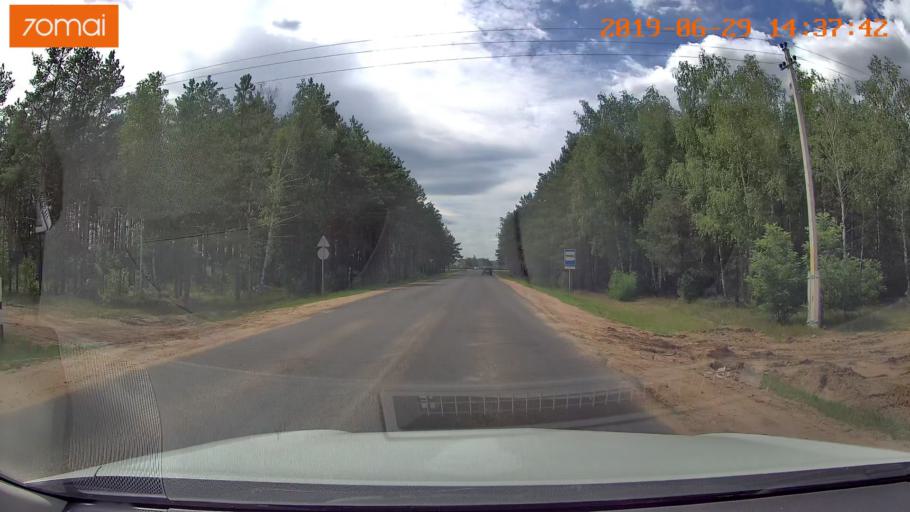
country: BY
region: Minsk
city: Starobin
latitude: 52.7509
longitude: 27.4641
